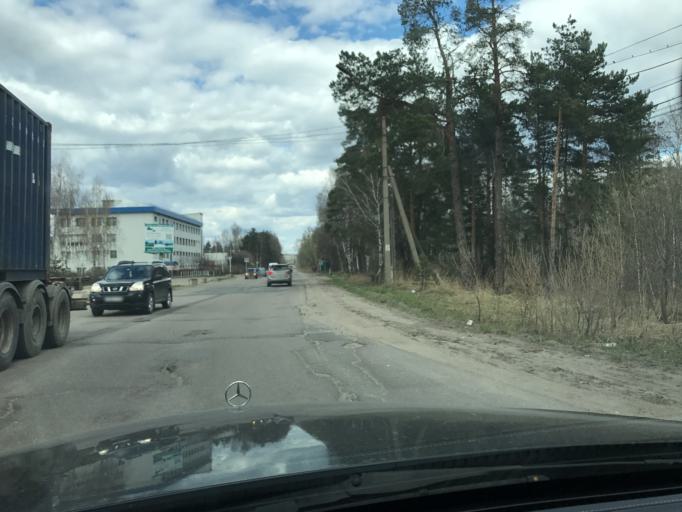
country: RU
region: Vladimir
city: Pokrov
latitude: 55.9036
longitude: 39.1914
